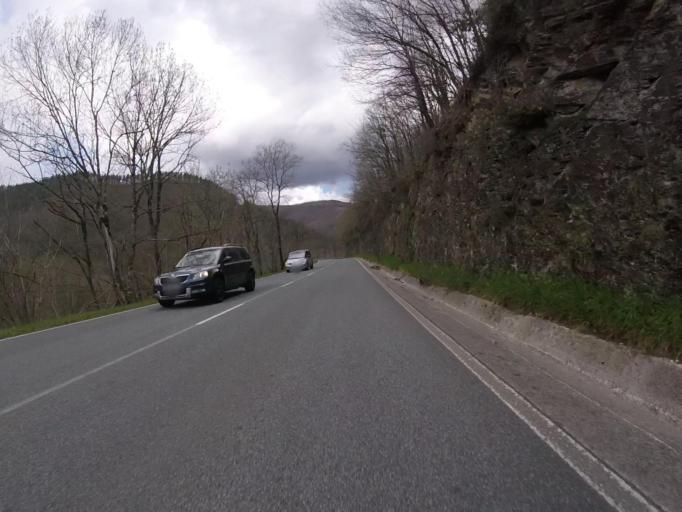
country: ES
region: Navarre
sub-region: Provincia de Navarra
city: Etxalar
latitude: 43.2359
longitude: -1.6591
